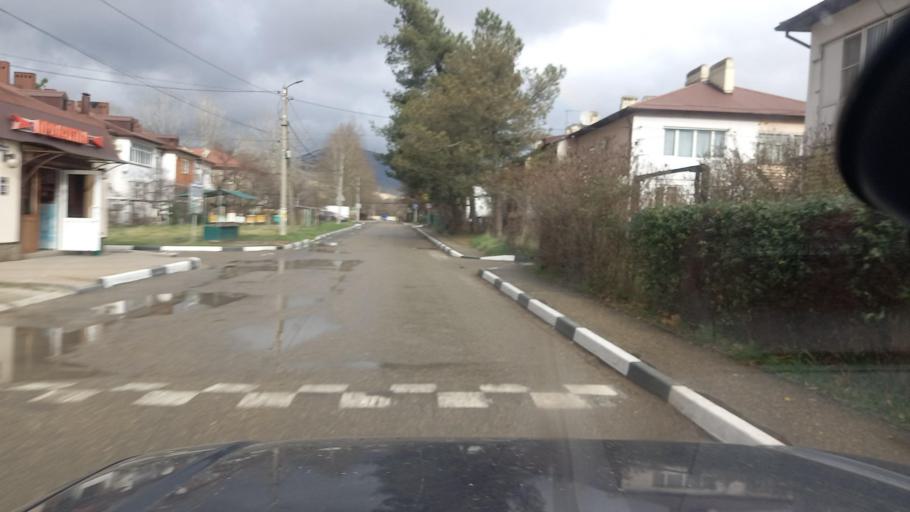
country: RU
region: Krasnodarskiy
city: Pshada
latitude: 44.4750
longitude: 38.3987
